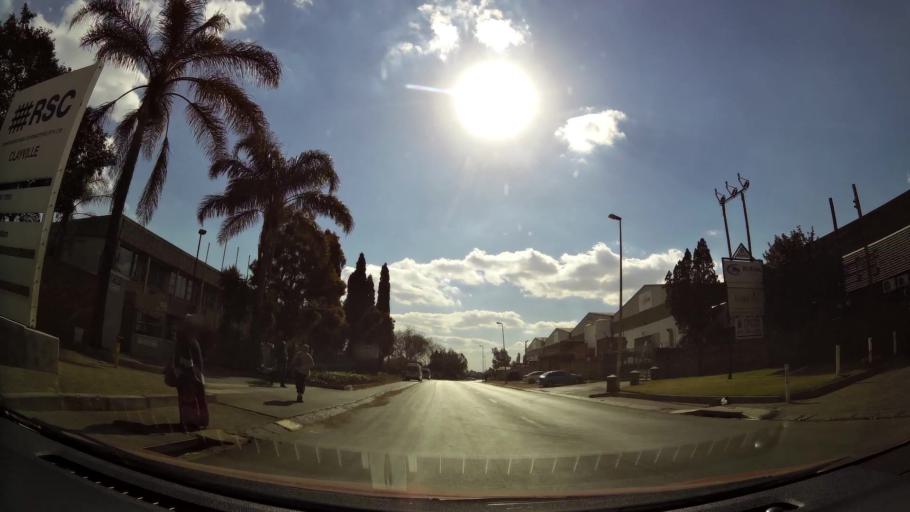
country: ZA
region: Gauteng
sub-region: Ekurhuleni Metropolitan Municipality
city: Tembisa
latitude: -25.9667
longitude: 28.2331
